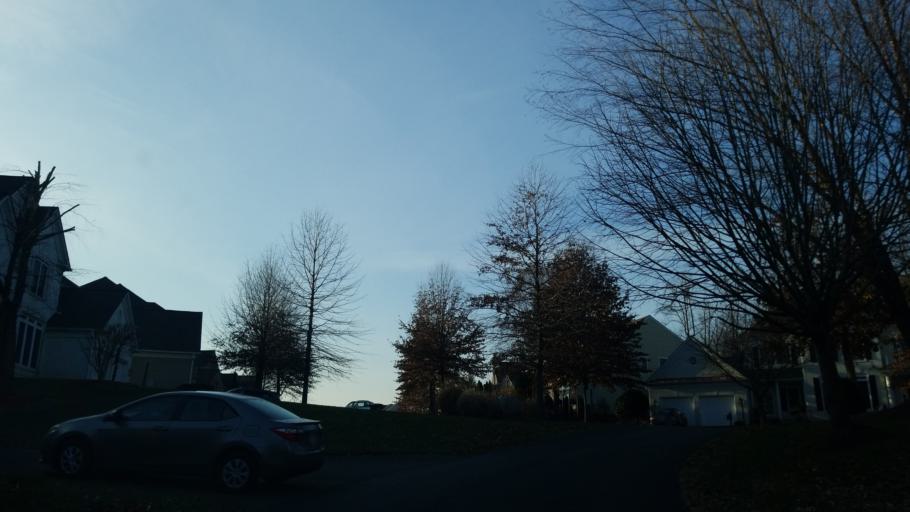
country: US
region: Virginia
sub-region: Fairfax County
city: Greenbriar
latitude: 38.8509
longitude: -77.3915
